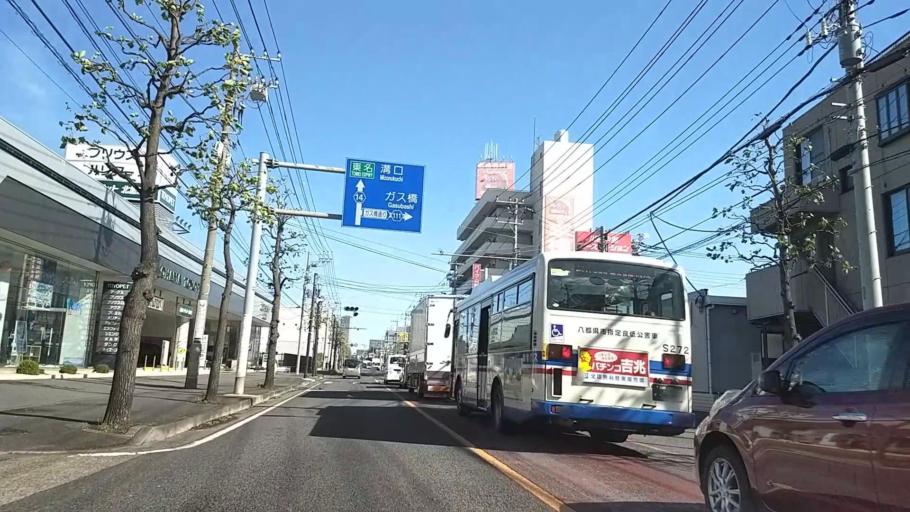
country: JP
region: Kanagawa
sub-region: Kawasaki-shi
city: Kawasaki
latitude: 35.5535
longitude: 139.6592
